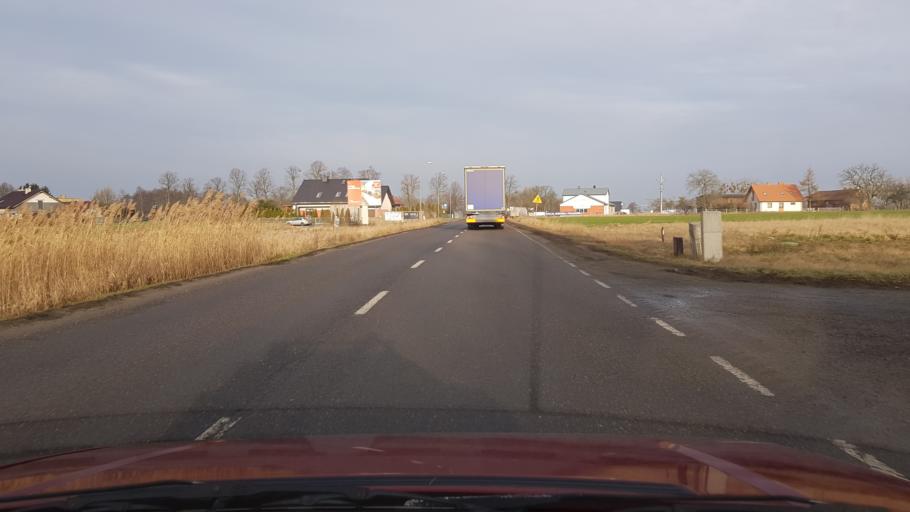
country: PL
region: West Pomeranian Voivodeship
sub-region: Powiat policki
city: Police
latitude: 53.5078
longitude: 14.5715
